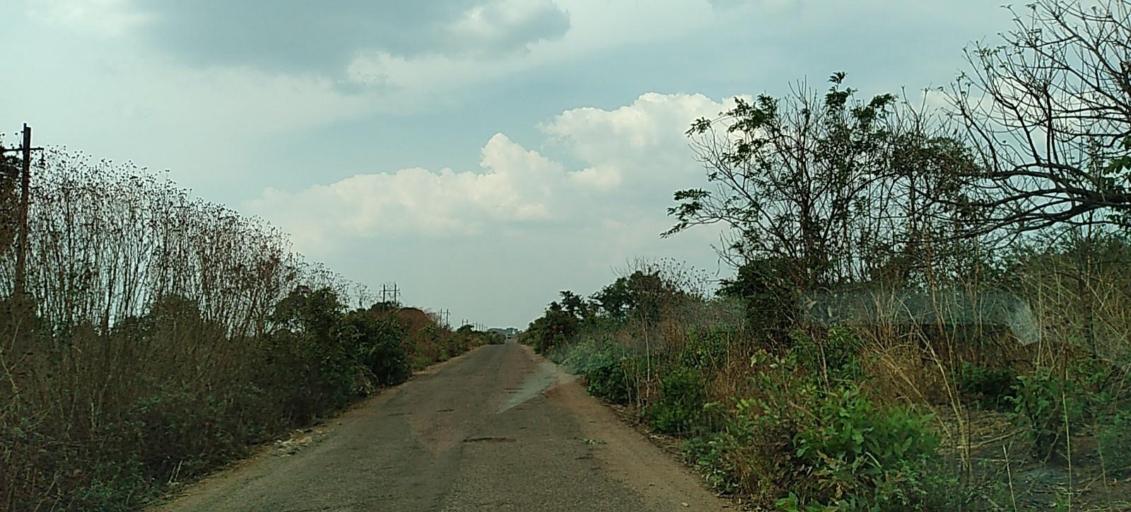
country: ZM
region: Copperbelt
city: Chililabombwe
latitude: -12.3825
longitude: 27.8107
